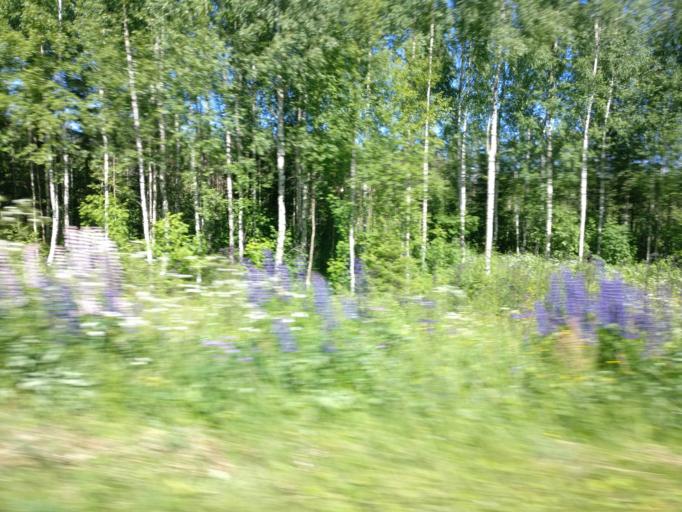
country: FI
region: Southern Savonia
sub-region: Savonlinna
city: Rantasalmi
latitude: 62.0315
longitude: 28.3393
